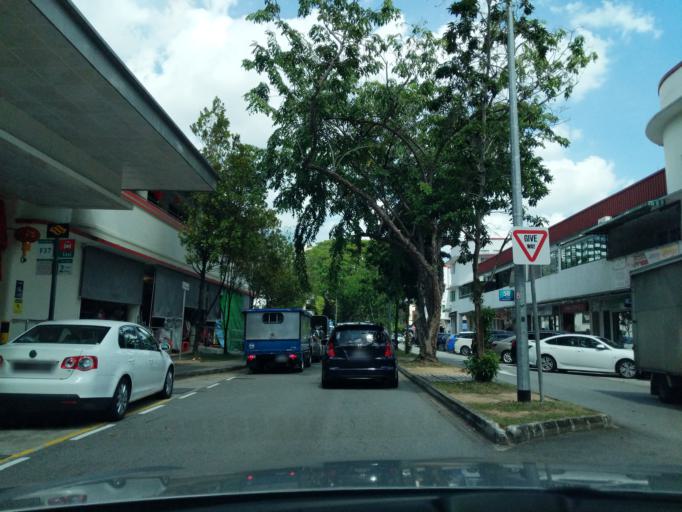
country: SG
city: Singapore
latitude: 1.2846
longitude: 103.8324
